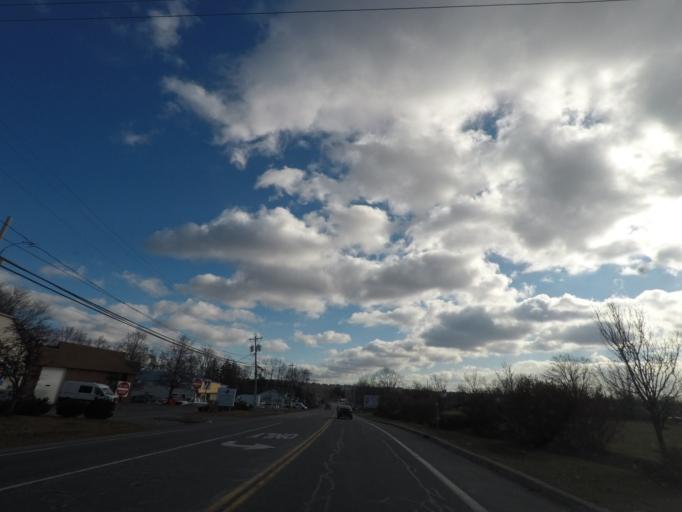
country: US
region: New York
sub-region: Schenectady County
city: Schenectady
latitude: 42.8392
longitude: -73.9377
